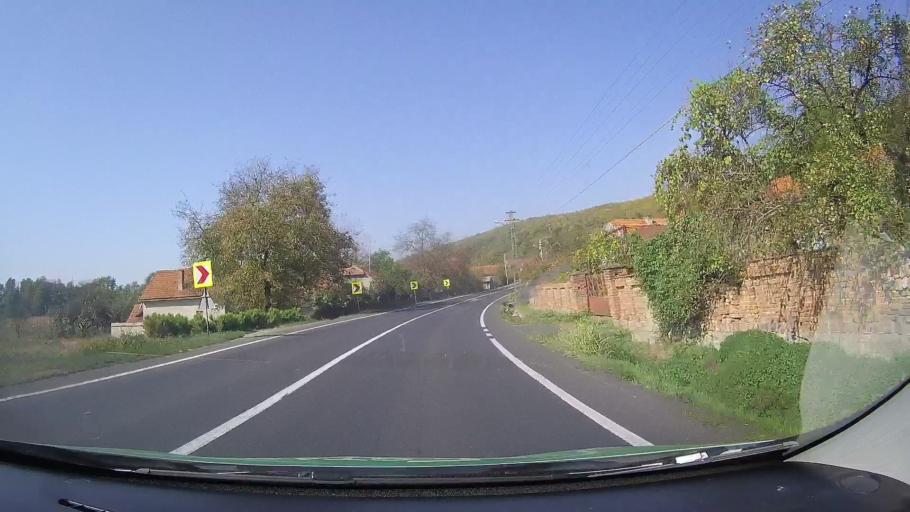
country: RO
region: Hunedoara
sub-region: Comuna Dobra
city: Dobra
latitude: 45.9387
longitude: 22.5416
